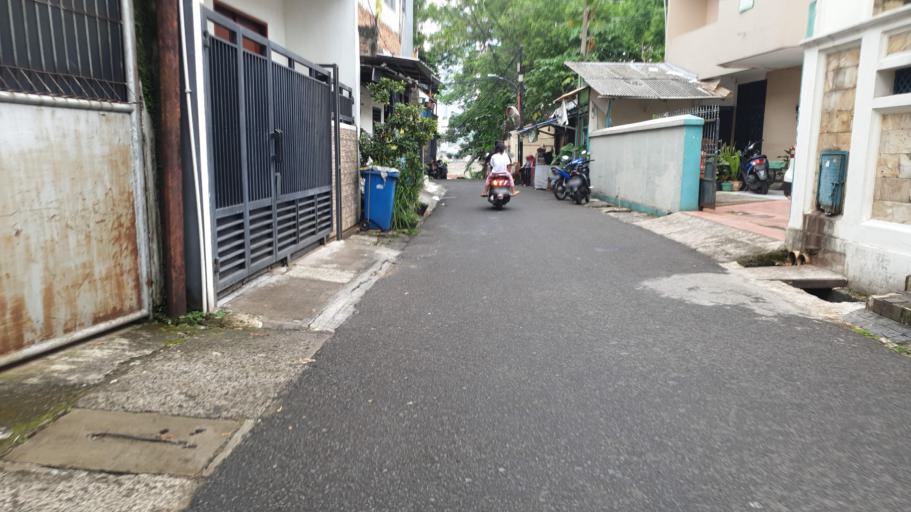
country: ID
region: Jakarta Raya
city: Jakarta
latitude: -6.2600
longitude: 106.7868
